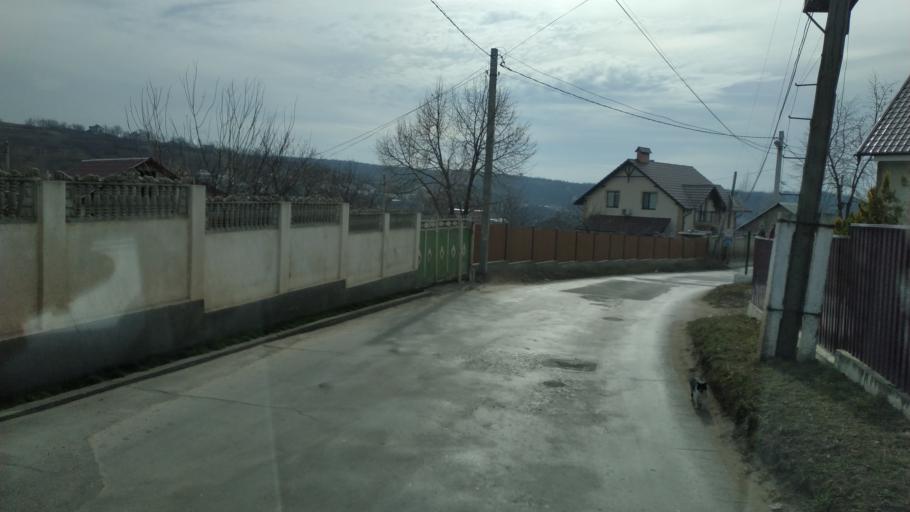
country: MD
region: Chisinau
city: Vatra
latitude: 47.0945
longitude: 28.7671
